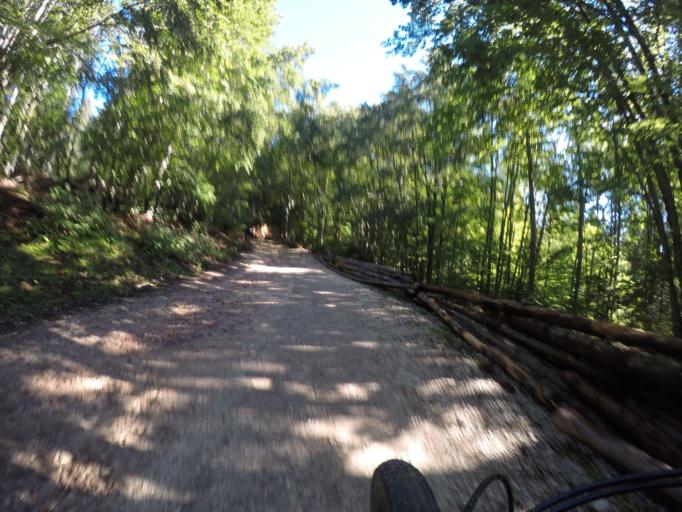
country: IT
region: Veneto
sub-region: Provincia di Vicenza
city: Canove di Roana
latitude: 45.8936
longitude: 11.4820
